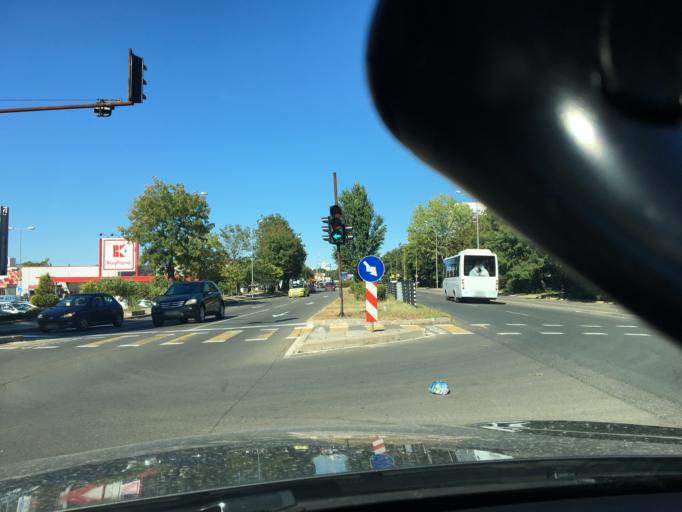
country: BG
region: Burgas
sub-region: Obshtina Burgas
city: Burgas
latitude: 42.5149
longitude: 27.4520
